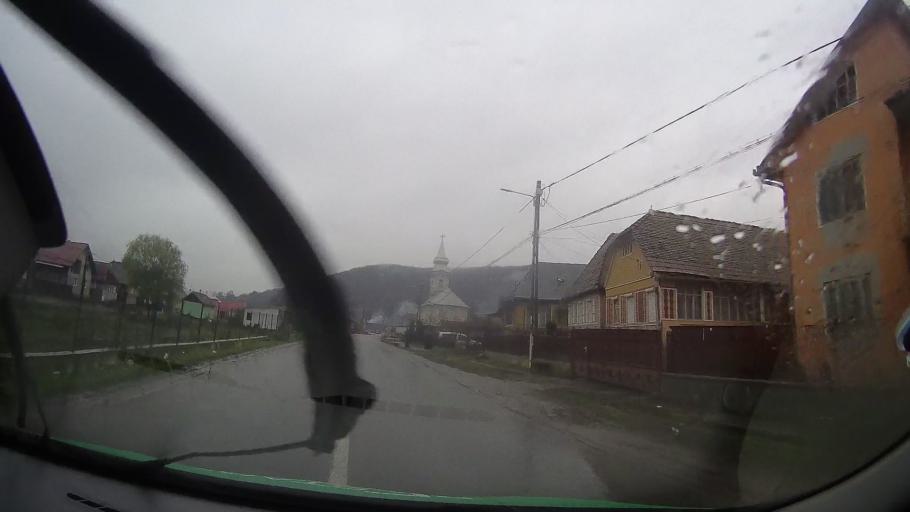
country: RO
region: Bistrita-Nasaud
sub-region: Comuna Sieut
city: Sieut
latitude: 46.9756
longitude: 24.6496
